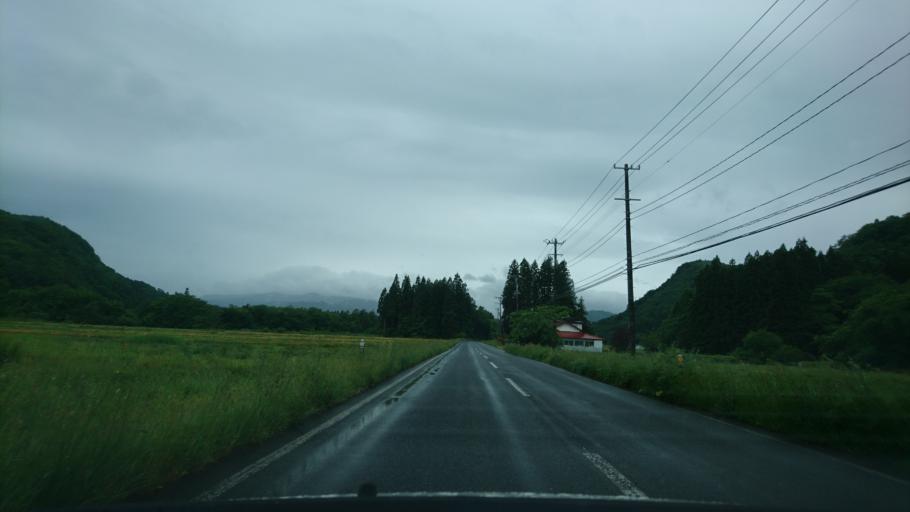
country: JP
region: Iwate
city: Ichinoseki
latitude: 38.9714
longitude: 140.9773
